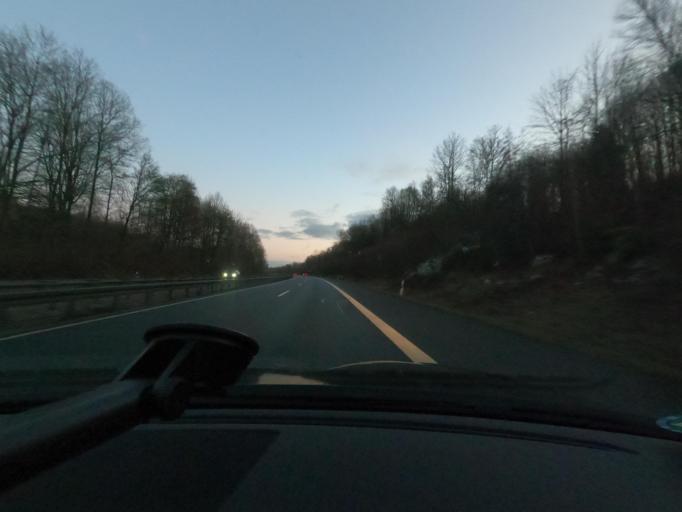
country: DE
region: Lower Saxony
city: Hoerden
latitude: 51.6951
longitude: 10.2888
